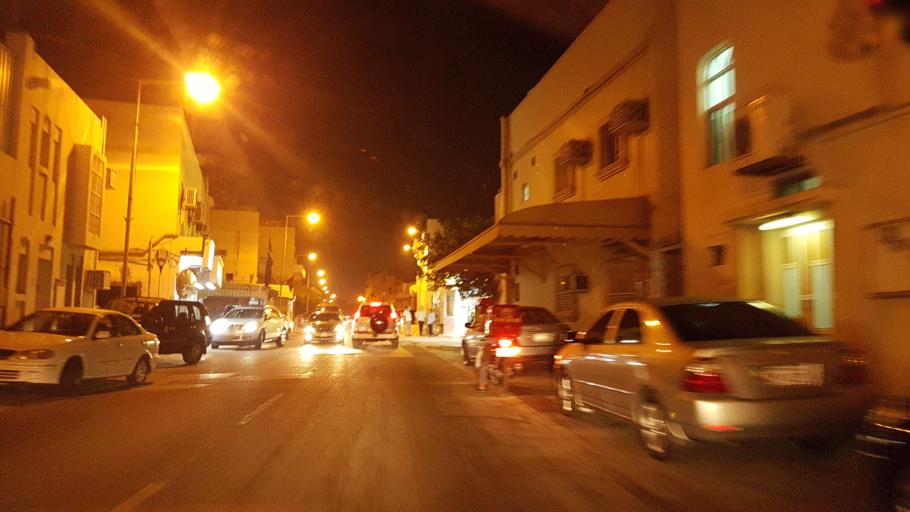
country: BH
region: Manama
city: Jidd Hafs
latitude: 26.2271
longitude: 50.5172
